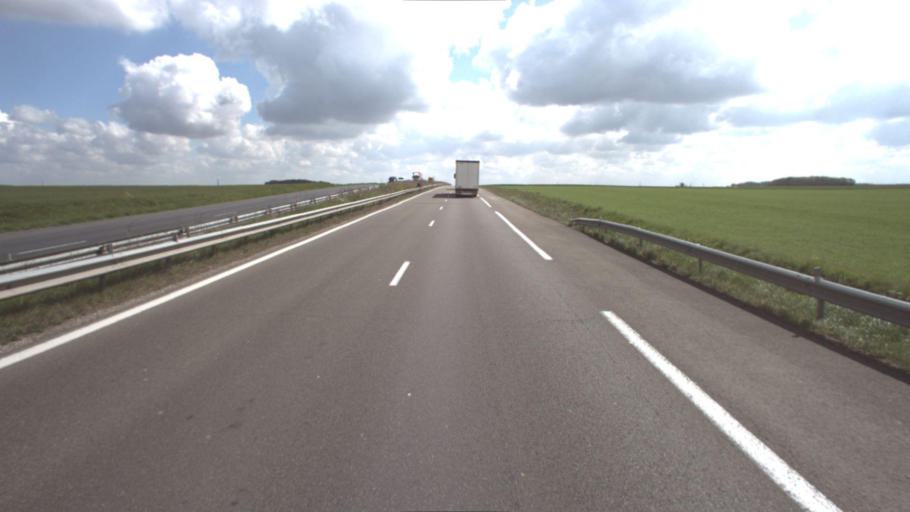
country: FR
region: Ile-de-France
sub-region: Departement de Seine-et-Marne
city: Touquin
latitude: 48.6853
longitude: 3.0368
